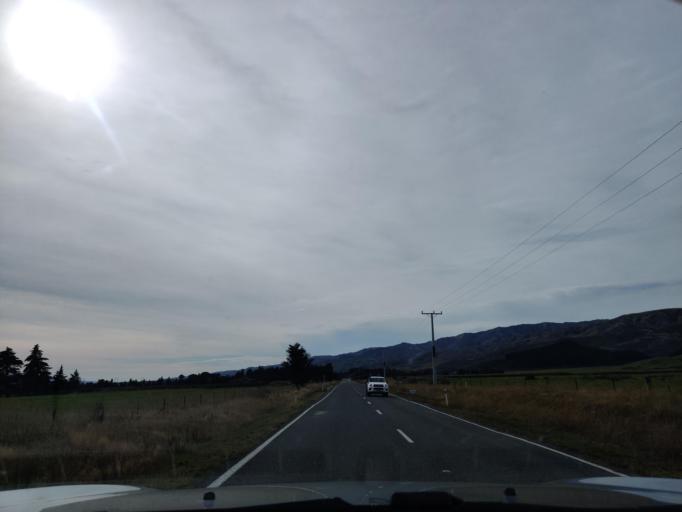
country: NZ
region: Tasman
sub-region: Tasman District
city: Brightwater
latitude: -41.6532
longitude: 173.2576
